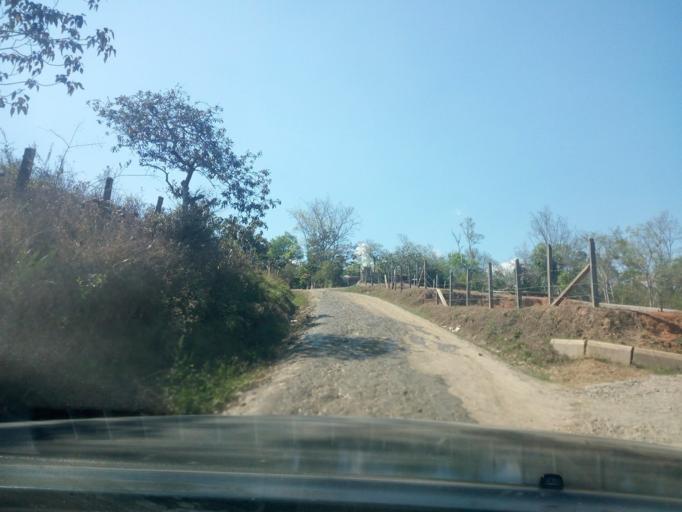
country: CO
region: Boyaca
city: Guateque
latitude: 5.0007
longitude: -73.4683
